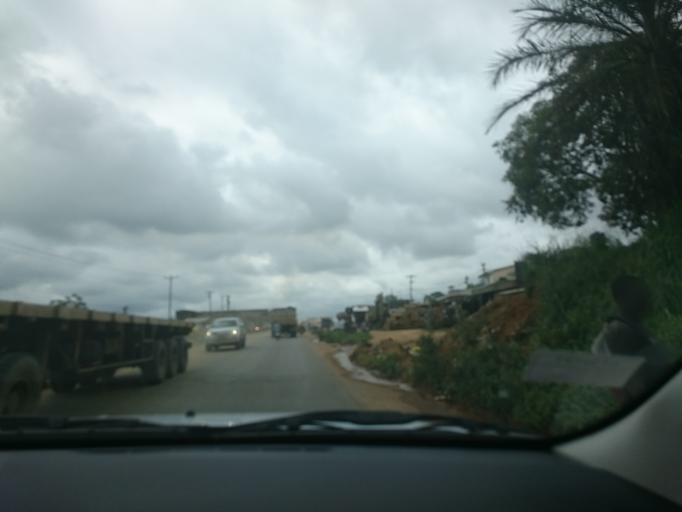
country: CM
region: Littoral
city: Douala
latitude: 3.9959
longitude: 9.7808
